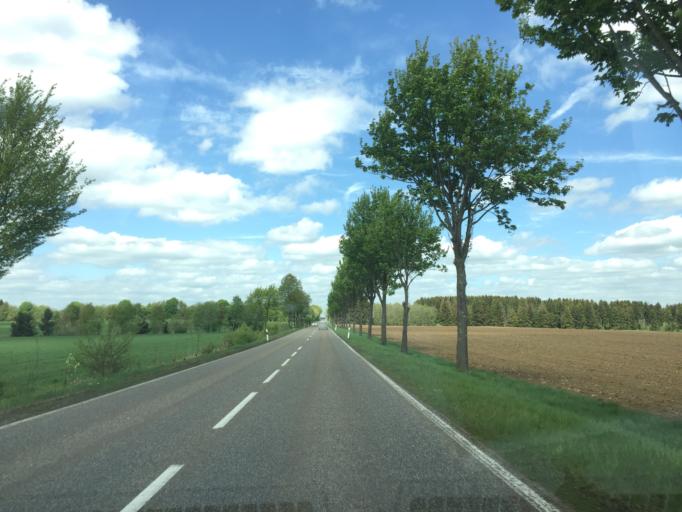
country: DE
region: Rheinland-Pfalz
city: Ailertchen
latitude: 50.6040
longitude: 7.9383
